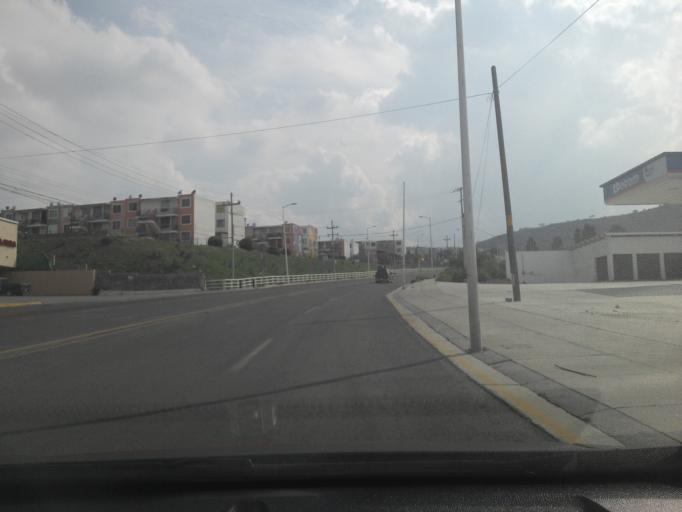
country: MX
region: Jalisco
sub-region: Tlajomulco de Zuniga
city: Lomas del Sur
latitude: 20.4932
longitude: -103.4180
